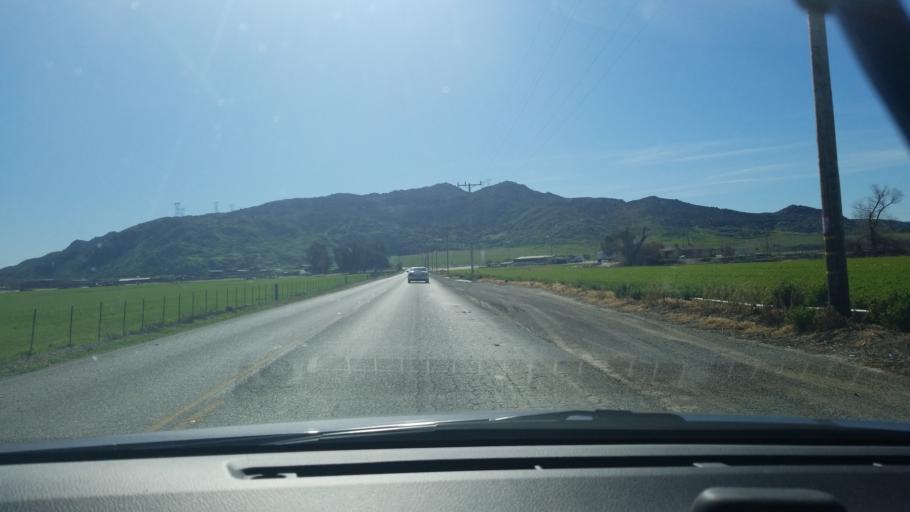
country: US
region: California
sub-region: Riverside County
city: Lakeview
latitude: 33.8509
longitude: -117.0685
